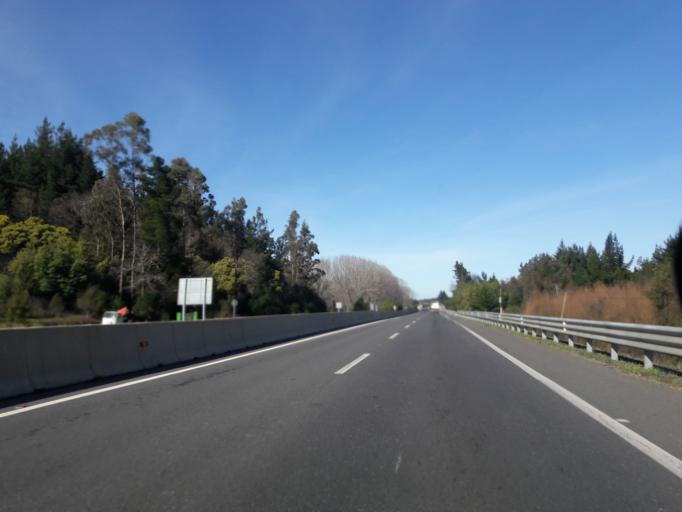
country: CL
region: Biobio
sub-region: Provincia de Biobio
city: Yumbel
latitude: -36.9440
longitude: -72.7548
